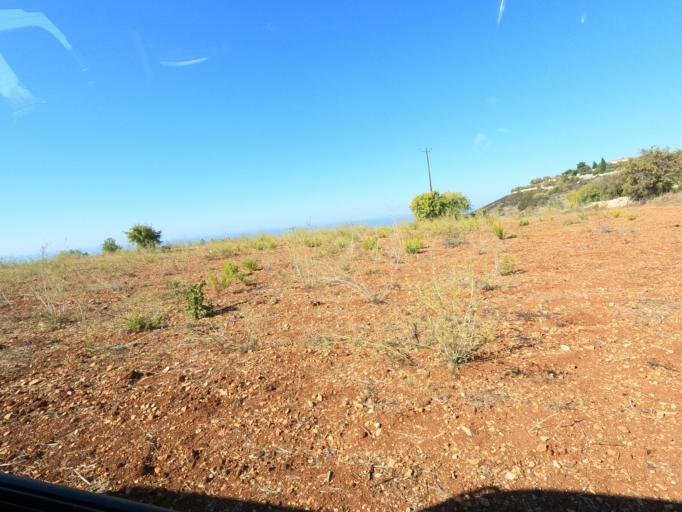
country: CY
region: Pafos
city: Mesogi
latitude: 34.8015
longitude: 32.4887
